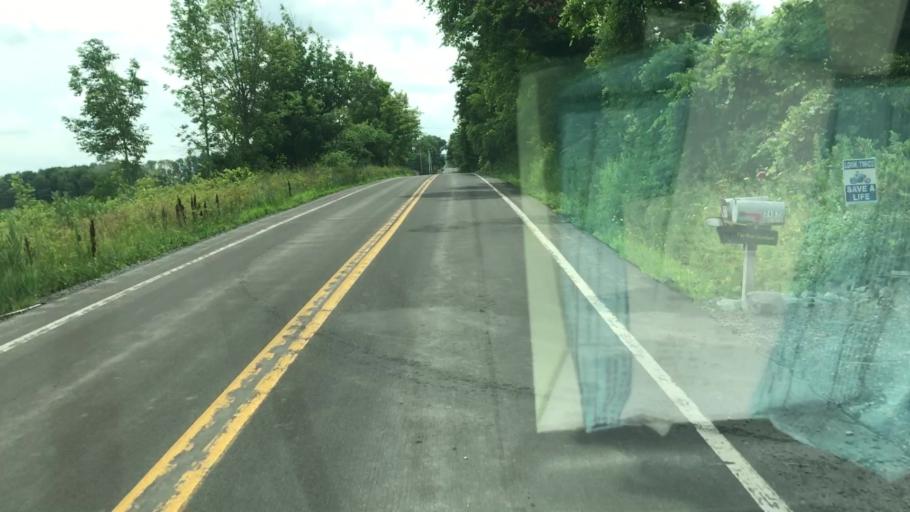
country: US
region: New York
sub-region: Onondaga County
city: Manlius
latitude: 42.9362
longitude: -75.9769
